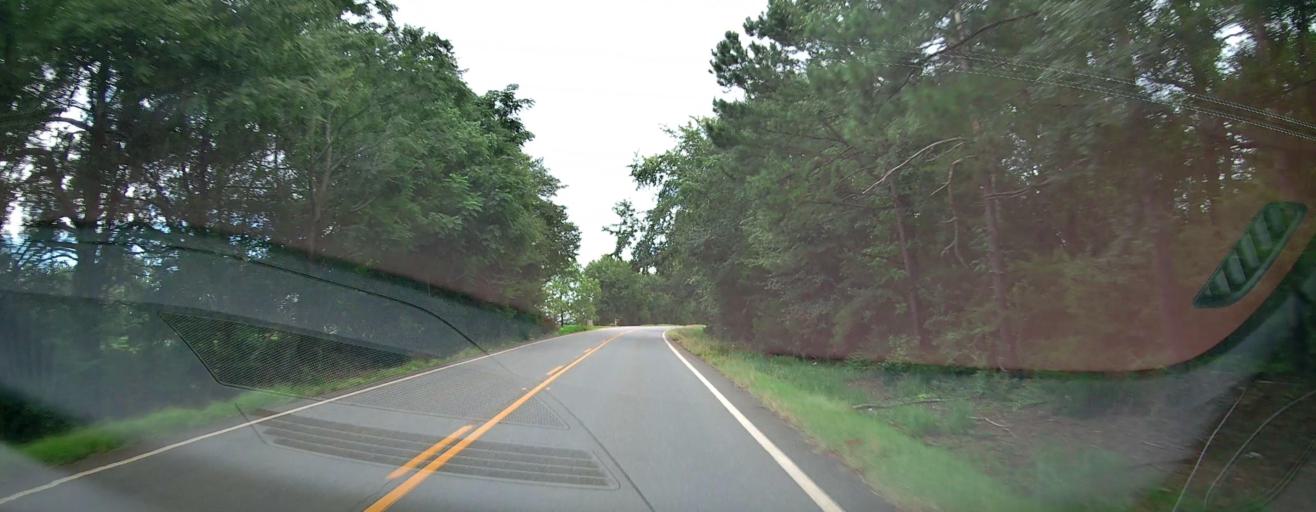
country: US
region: Georgia
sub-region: Marion County
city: Buena Vista
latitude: 32.2600
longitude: -84.4221
